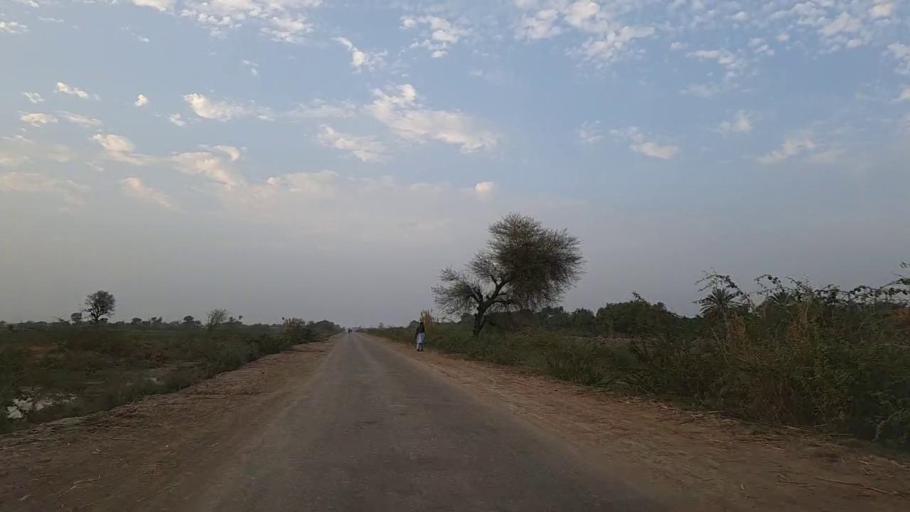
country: PK
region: Sindh
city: Mirwah Gorchani
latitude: 25.3213
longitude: 69.2192
